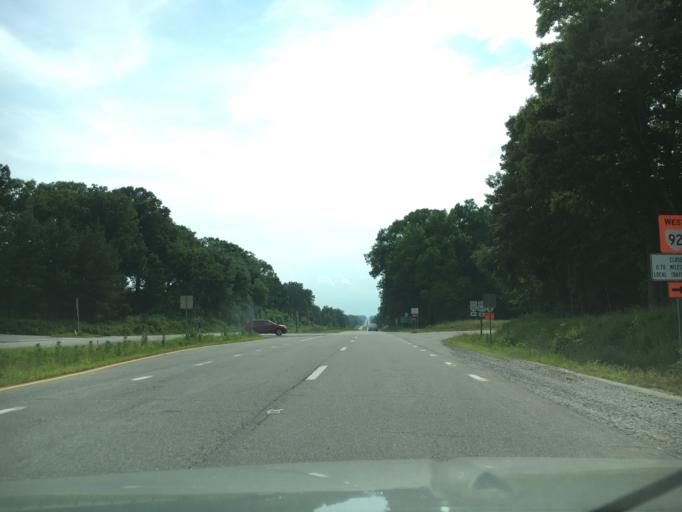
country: US
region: Virginia
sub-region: Mecklenburg County
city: Chase City
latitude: 36.8345
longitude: -78.6569
